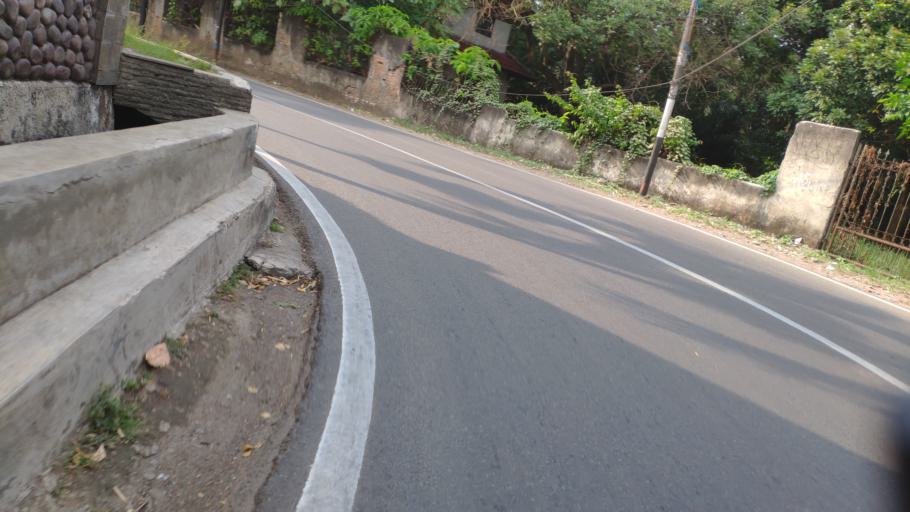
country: ID
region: West Java
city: Pamulang
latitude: -6.3160
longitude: 106.8134
